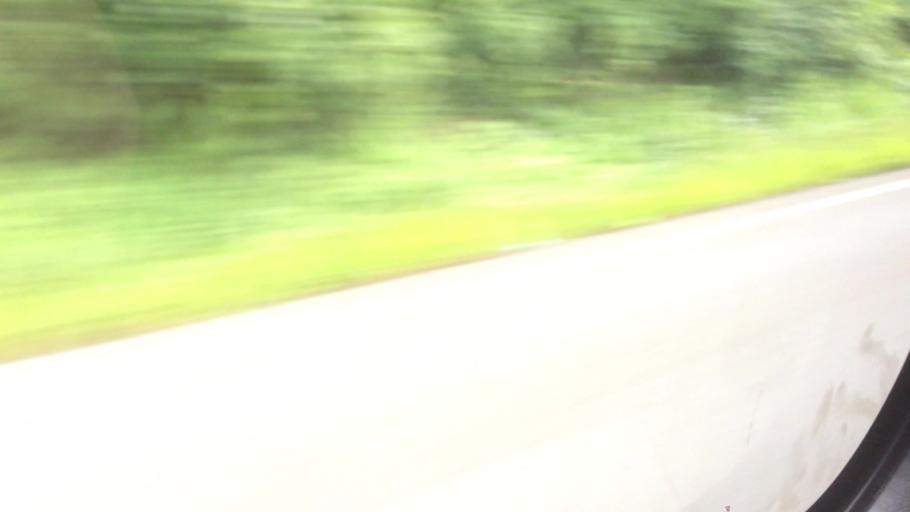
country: US
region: New York
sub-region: Dutchess County
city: Tivoli
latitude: 42.0411
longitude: -73.8946
